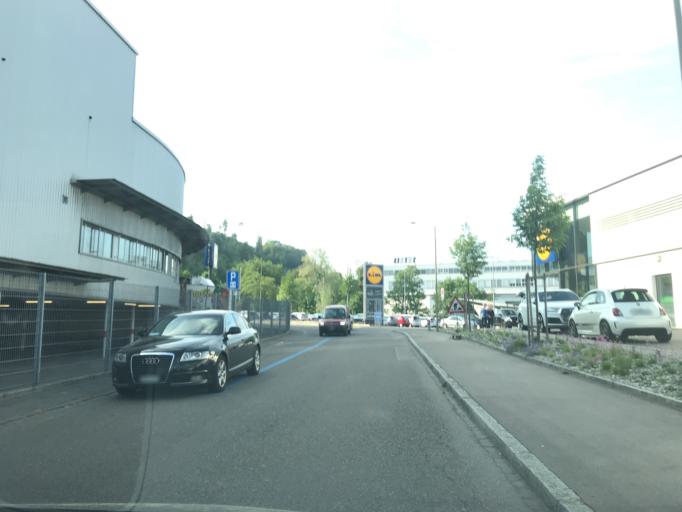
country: CH
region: Zurich
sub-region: Bezirk Winterthur
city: Toess (Kreis 4) / Eichliacker
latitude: 47.4858
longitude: 8.7040
